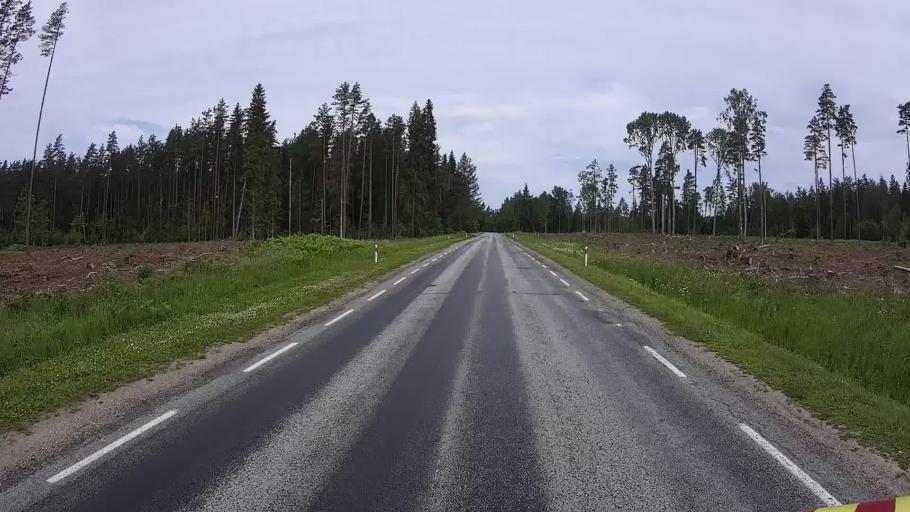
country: EE
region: Viljandimaa
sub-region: Karksi vald
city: Karksi-Nuia
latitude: 58.2204
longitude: 25.6170
